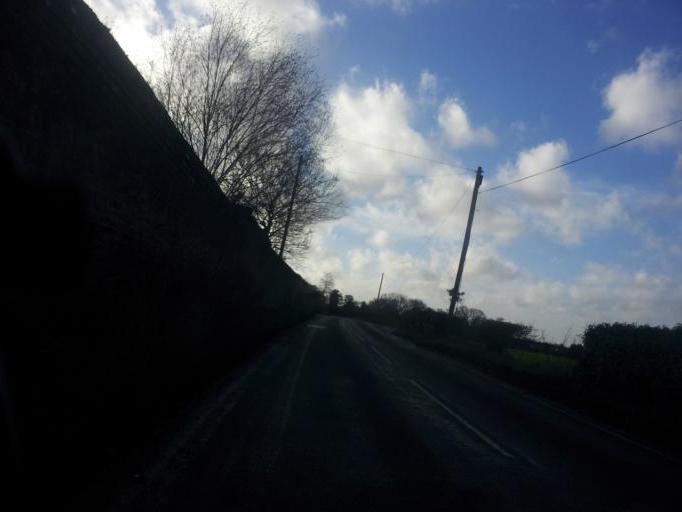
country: GB
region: England
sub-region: Kent
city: Meopham
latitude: 51.3797
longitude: 0.3715
